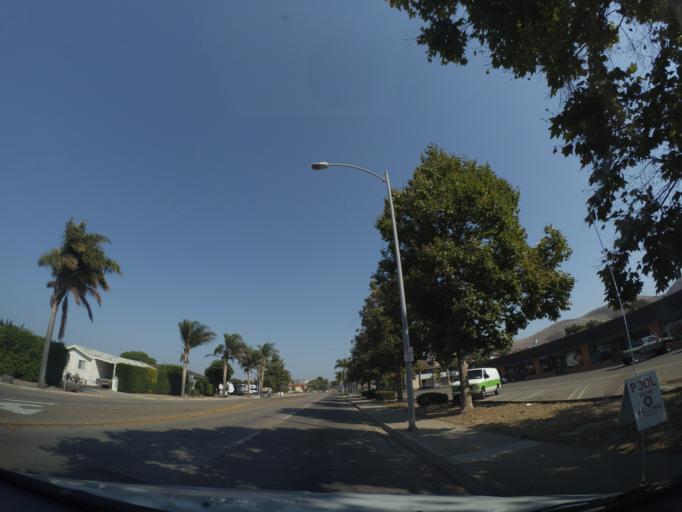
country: US
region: California
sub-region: Santa Barbara County
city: Lompoc
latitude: 34.6389
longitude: -120.4484
